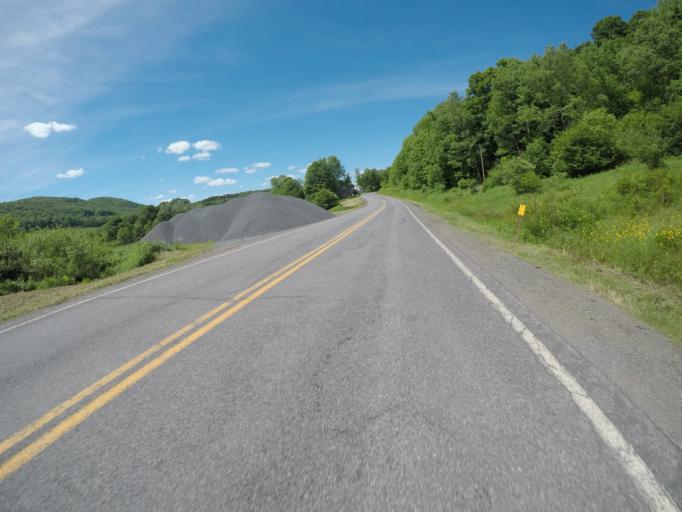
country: US
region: New York
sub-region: Delaware County
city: Delhi
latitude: 42.1548
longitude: -74.7979
